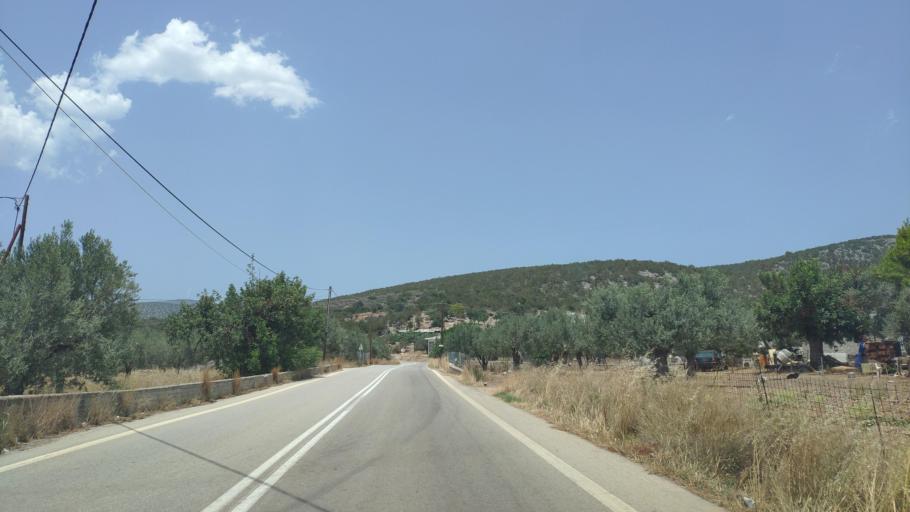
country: GR
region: Peloponnese
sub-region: Nomos Argolidos
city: Koilas
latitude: 37.4193
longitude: 23.1535
